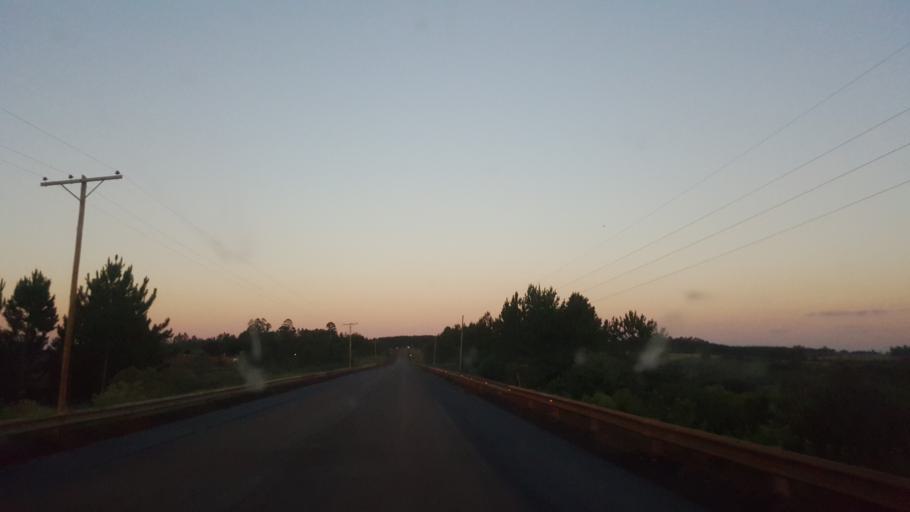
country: AR
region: Corrientes
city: Garruchos
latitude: -28.2326
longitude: -55.8127
